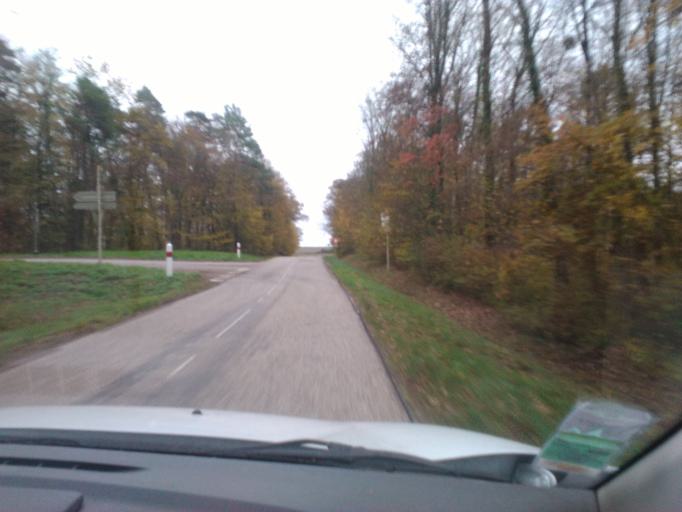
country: FR
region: Lorraine
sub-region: Departement des Vosges
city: Darnieulles
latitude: 48.2318
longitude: 6.2954
